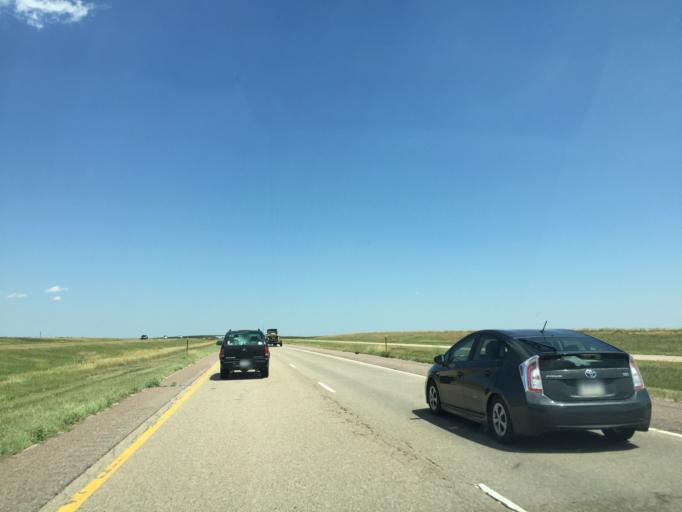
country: US
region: Colorado
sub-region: Lincoln County
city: Hugo
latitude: 39.2804
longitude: -103.3598
